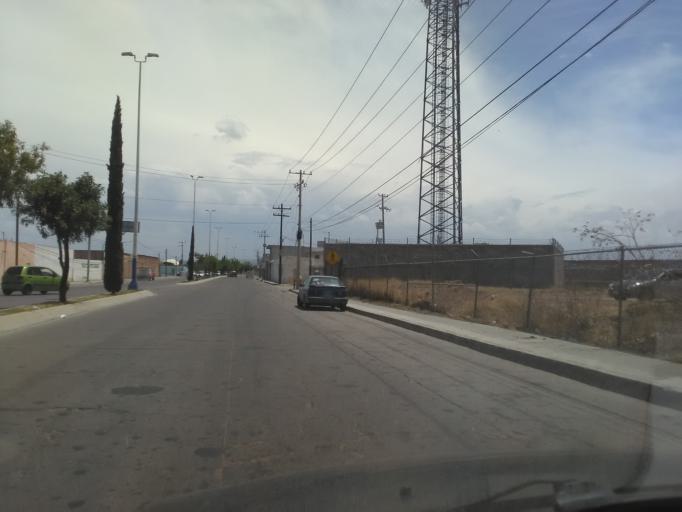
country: MX
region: Durango
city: Victoria de Durango
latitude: 24.0301
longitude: -104.6136
